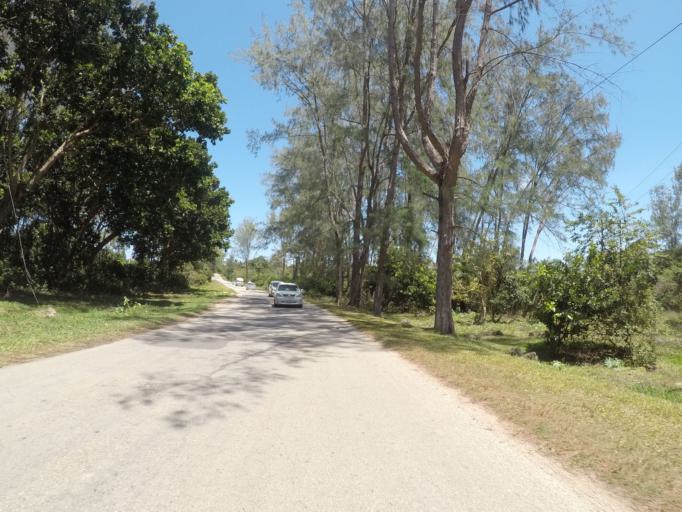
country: TZ
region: Zanzibar Central/South
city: Mahonda
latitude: -6.2778
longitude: 39.4152
